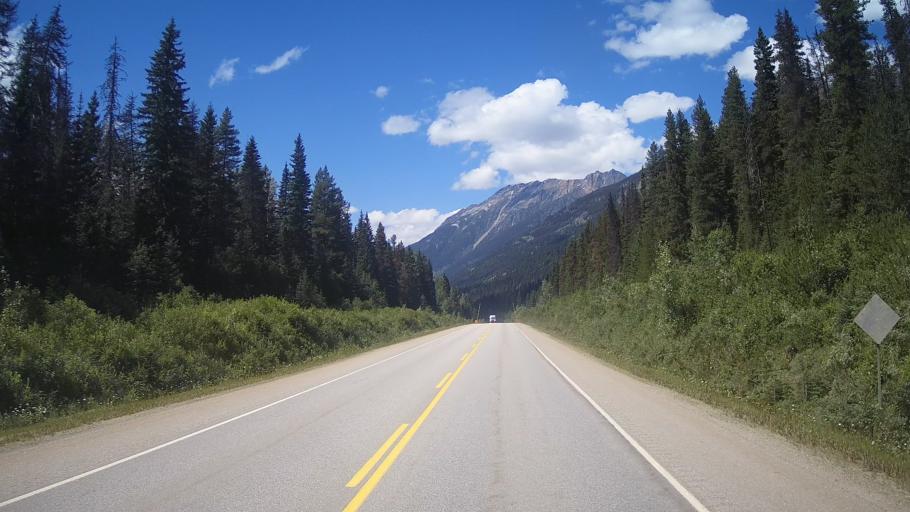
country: CA
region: Alberta
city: Grande Cache
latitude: 52.9946
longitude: -119.0196
